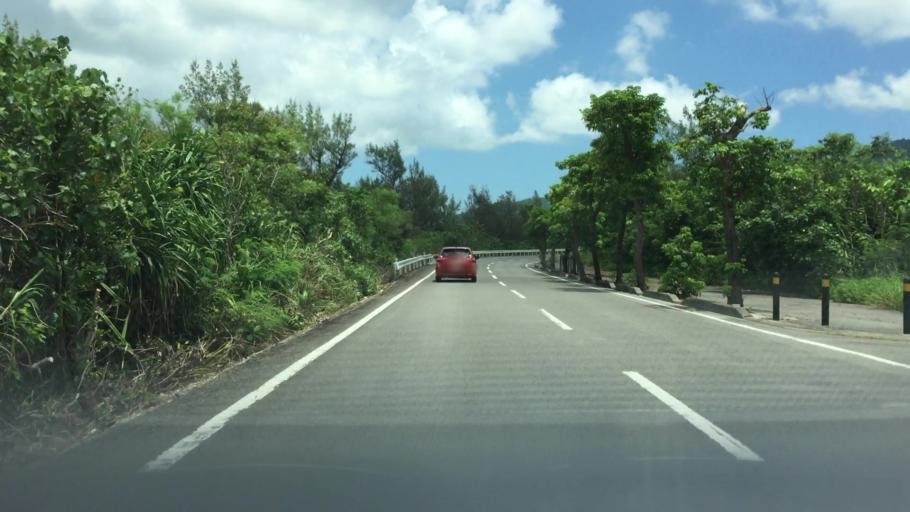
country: JP
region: Okinawa
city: Ishigaki
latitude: 24.3995
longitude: 124.1404
